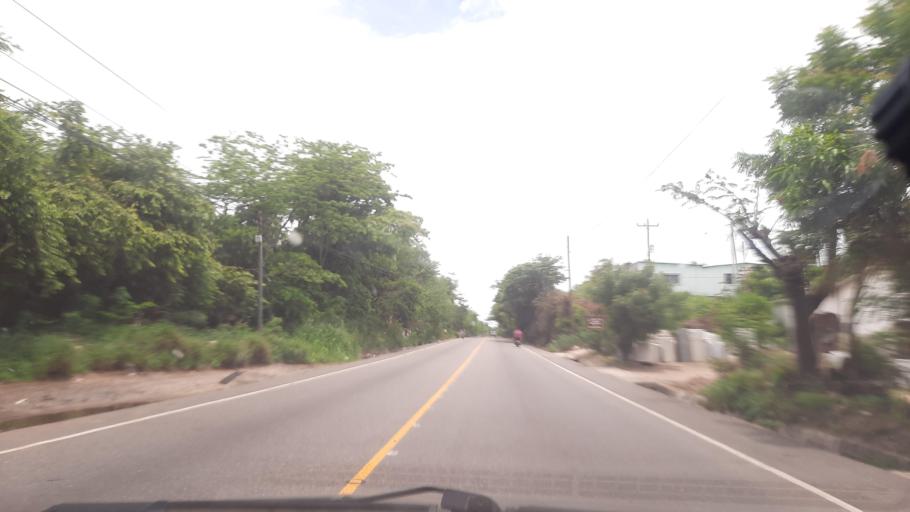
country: GT
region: Zacapa
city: Rio Hondo
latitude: 15.0623
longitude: -89.5348
